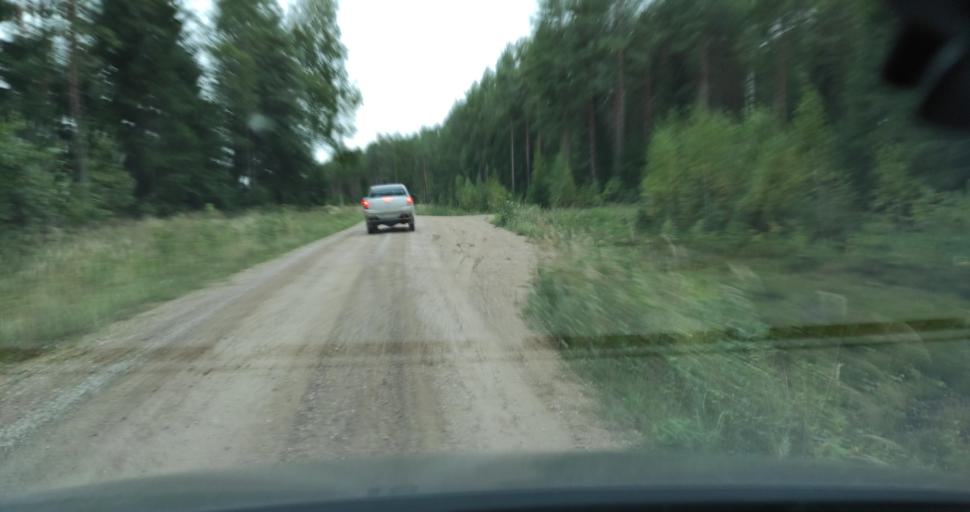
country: LV
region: Talsu Rajons
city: Sabile
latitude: 57.0217
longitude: 22.3540
